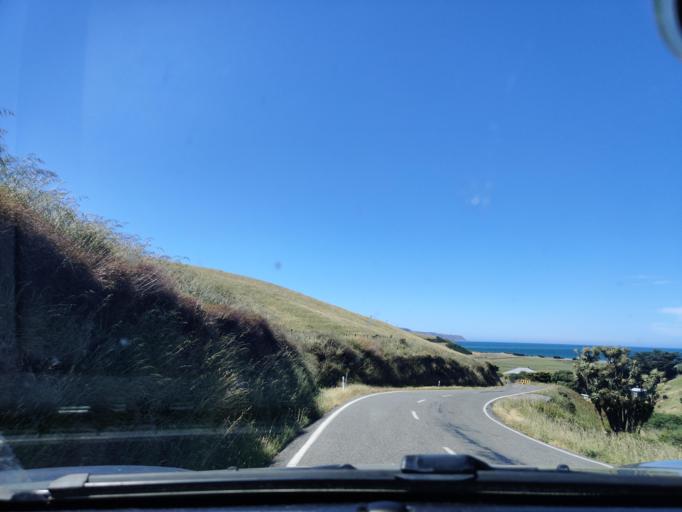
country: NZ
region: Wellington
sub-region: Upper Hutt City
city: Upper Hutt
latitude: -41.3988
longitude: 175.1768
